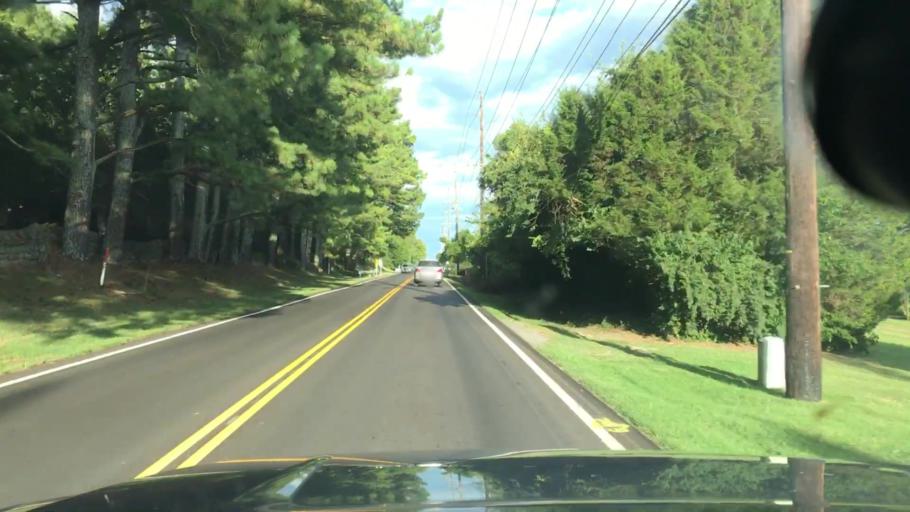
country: US
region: Tennessee
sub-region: Davidson County
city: Forest Hills
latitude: 36.0426
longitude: -86.8388
